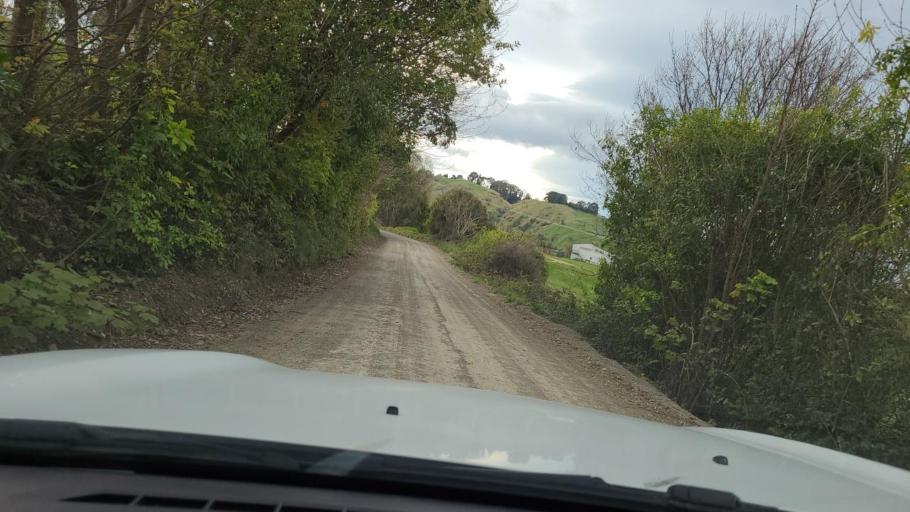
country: NZ
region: Hawke's Bay
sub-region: Napier City
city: Napier
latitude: -39.2869
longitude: 176.8428
